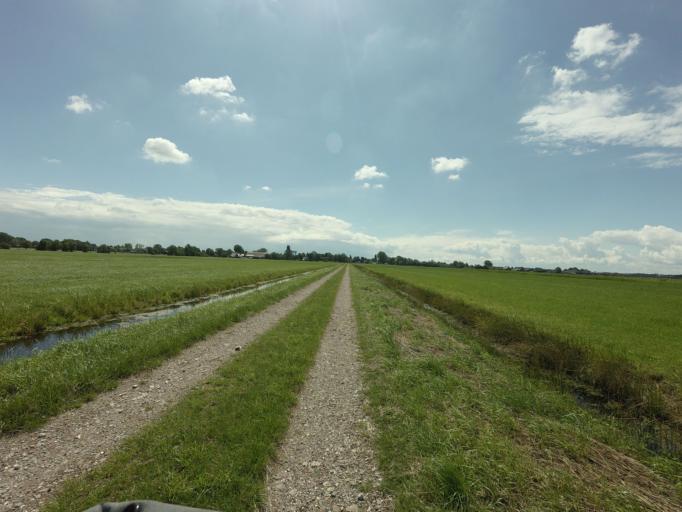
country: NL
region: South Holland
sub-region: Gemeente Schoonhoven
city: Schoonhoven
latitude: 51.9646
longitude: 4.8739
